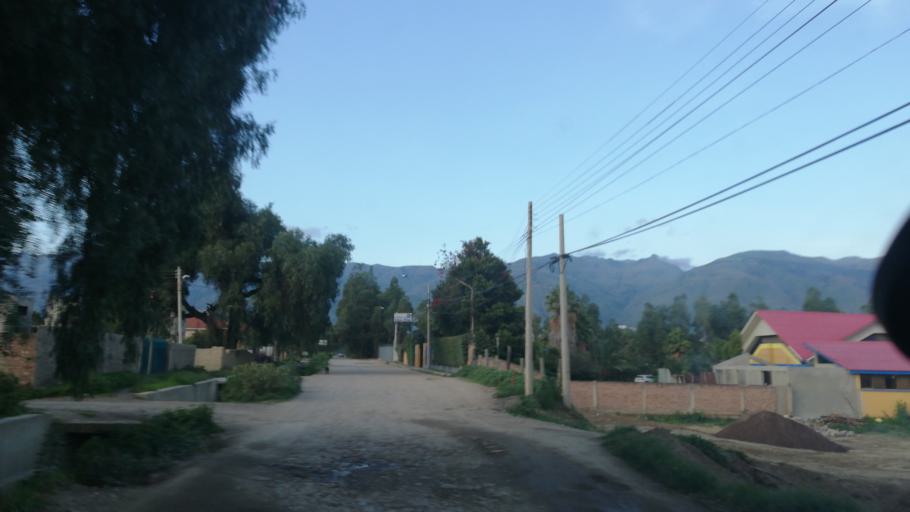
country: BO
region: Cochabamba
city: Cochabamba
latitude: -17.3791
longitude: -66.2075
